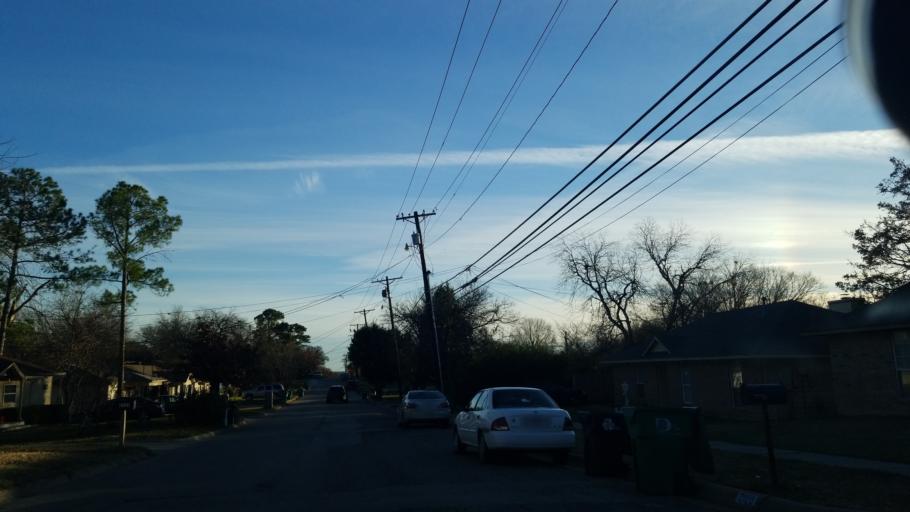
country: US
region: Texas
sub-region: Denton County
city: Denton
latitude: 33.1930
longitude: -97.1418
